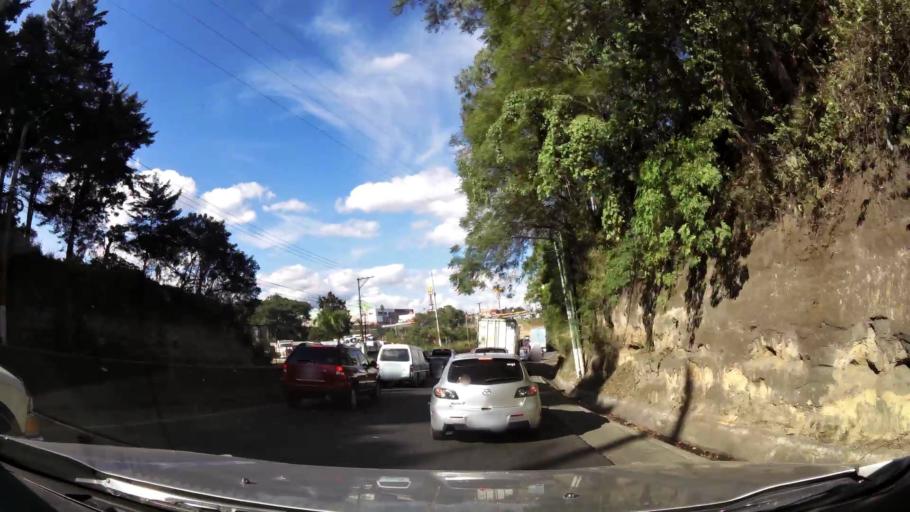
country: GT
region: Guatemala
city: Villa Nueva
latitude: 14.5274
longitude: -90.5968
